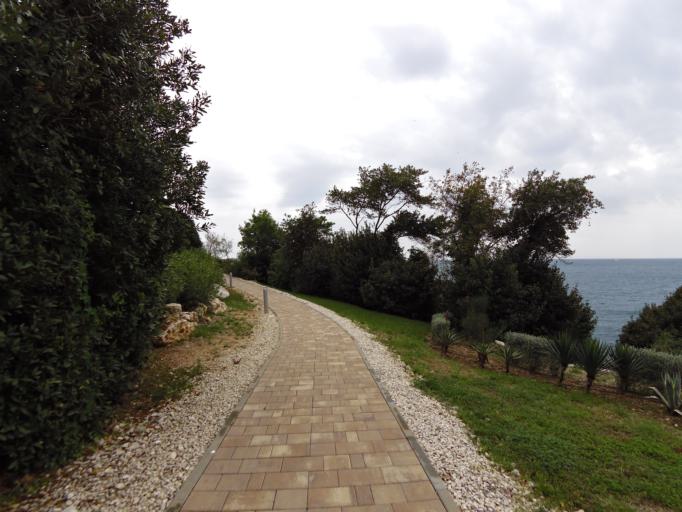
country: HR
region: Istarska
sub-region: Grad Porec
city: Porec
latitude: 45.2236
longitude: 13.5836
